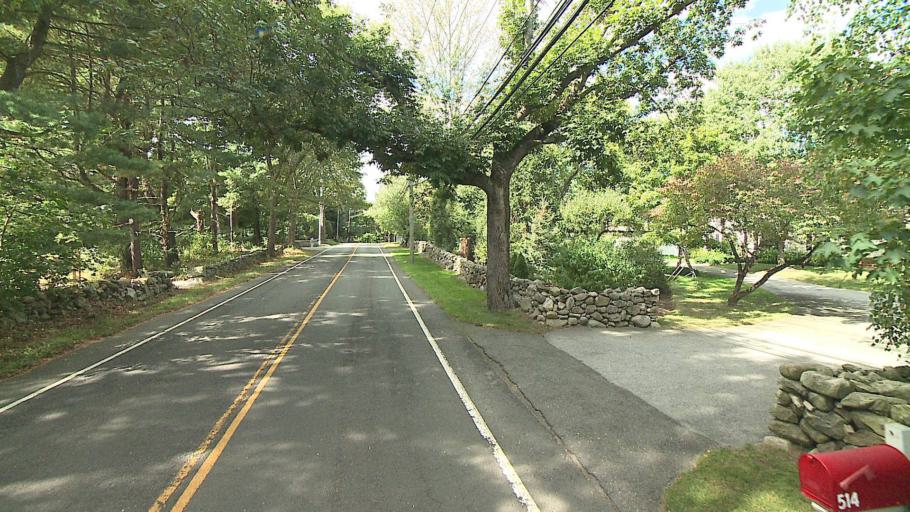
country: US
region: Connecticut
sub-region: Fairfield County
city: New Canaan
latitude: 41.1580
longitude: -73.4671
